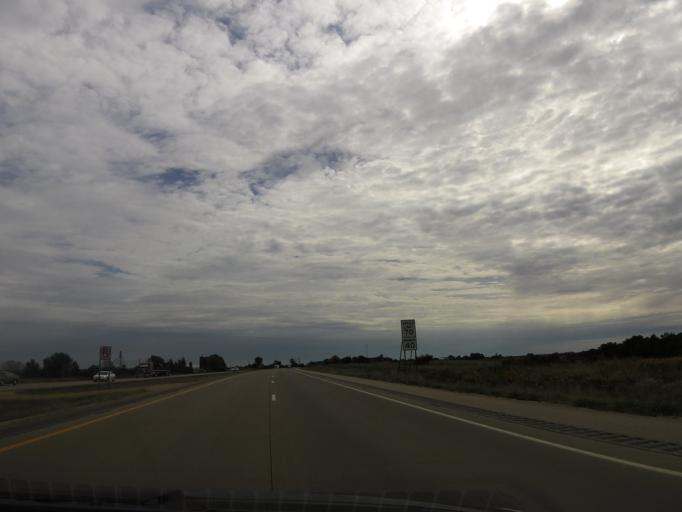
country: US
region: Minnesota
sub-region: Winona County
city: Winona
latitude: 43.9145
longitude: -91.5868
